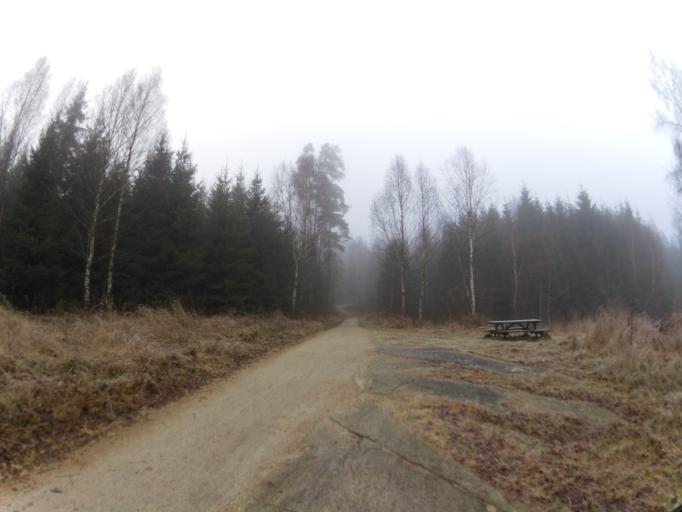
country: NO
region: Ostfold
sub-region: Fredrikstad
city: Fredrikstad
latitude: 59.2561
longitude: 10.9680
